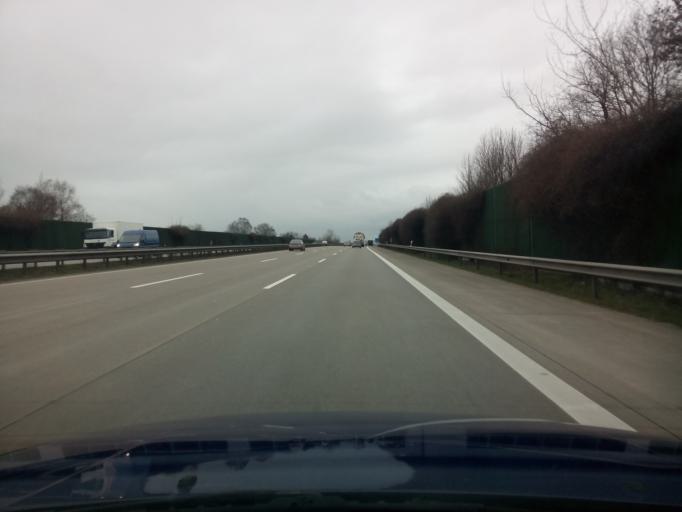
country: DE
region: Lower Saxony
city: Ritterhude
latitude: 53.1297
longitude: 8.7642
